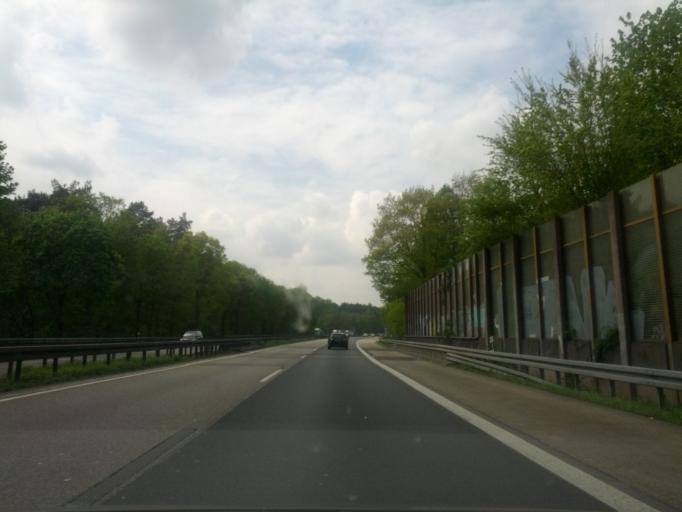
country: DE
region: North Rhine-Westphalia
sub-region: Regierungsbezirk Koln
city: Rath
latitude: 50.9478
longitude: 7.1188
